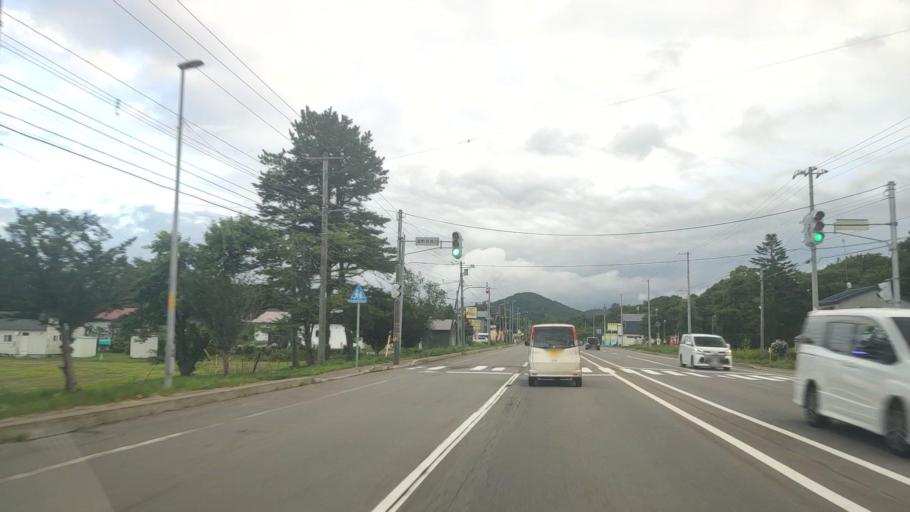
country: JP
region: Hokkaido
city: Nanae
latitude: 42.0039
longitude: 140.6332
